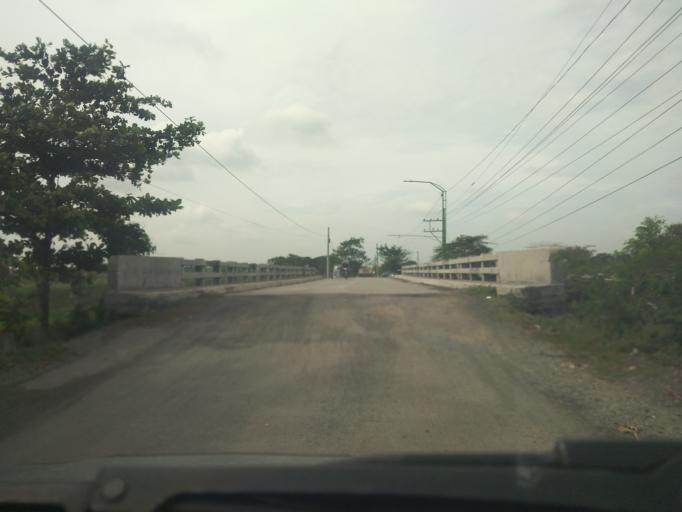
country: PH
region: Central Luzon
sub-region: Province of Pampanga
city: Pau
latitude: 15.0167
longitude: 120.7171
